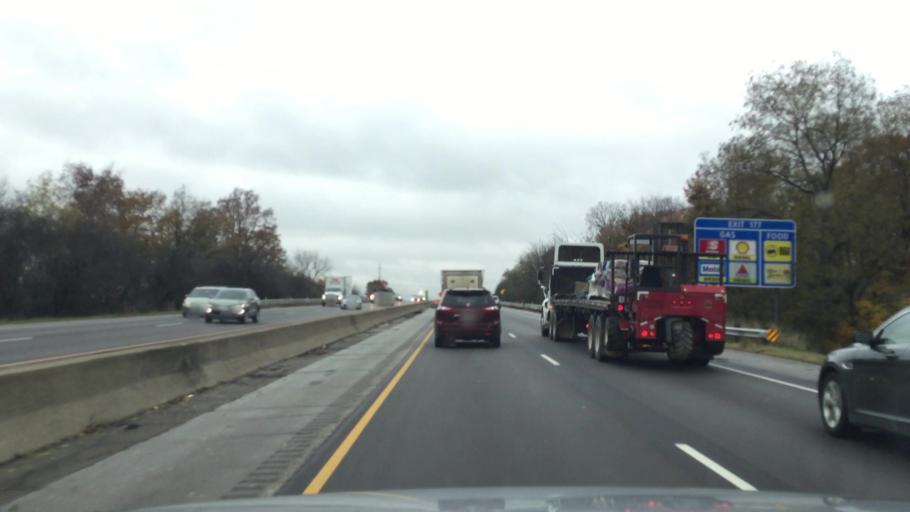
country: US
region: Michigan
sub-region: Washtenaw County
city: Ann Arbor
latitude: 42.2374
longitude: -83.7257
